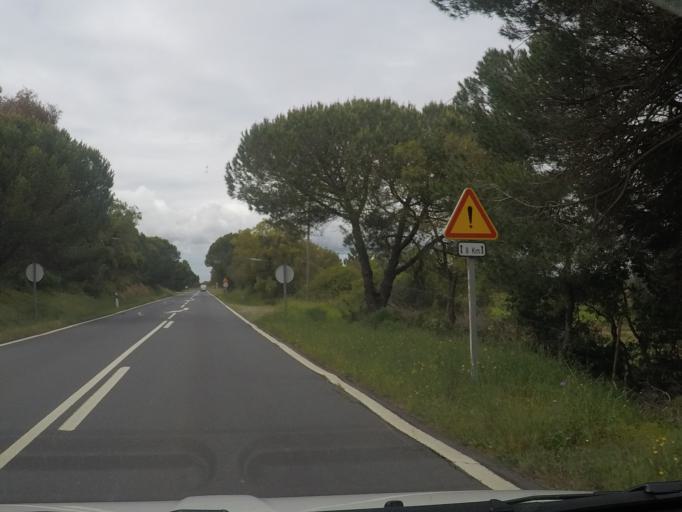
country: PT
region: Setubal
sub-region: Sines
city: Porto Covo
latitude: 37.8767
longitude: -8.7433
